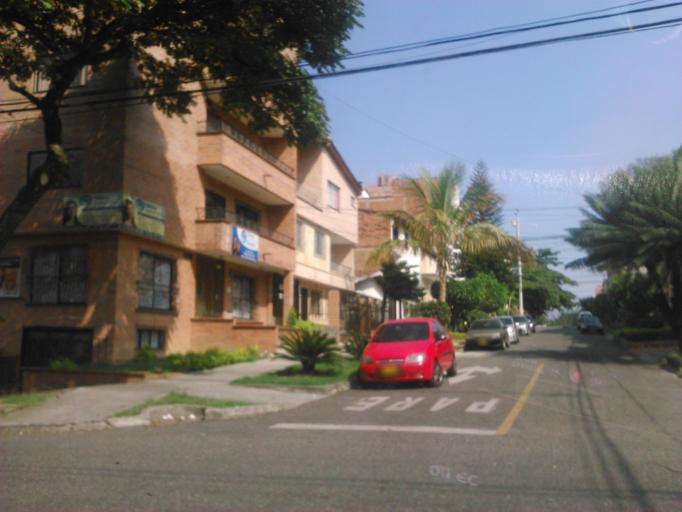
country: CO
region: Antioquia
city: Medellin
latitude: 6.2501
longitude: -75.6103
